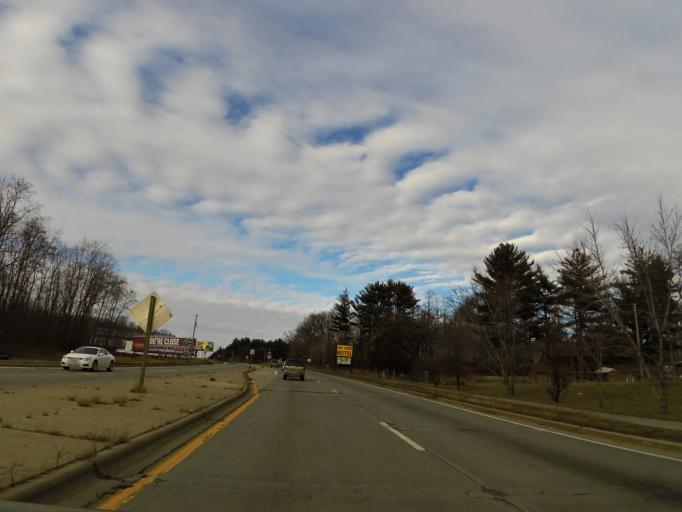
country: US
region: Wisconsin
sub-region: Sauk County
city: West Baraboo
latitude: 43.4780
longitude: -89.7689
